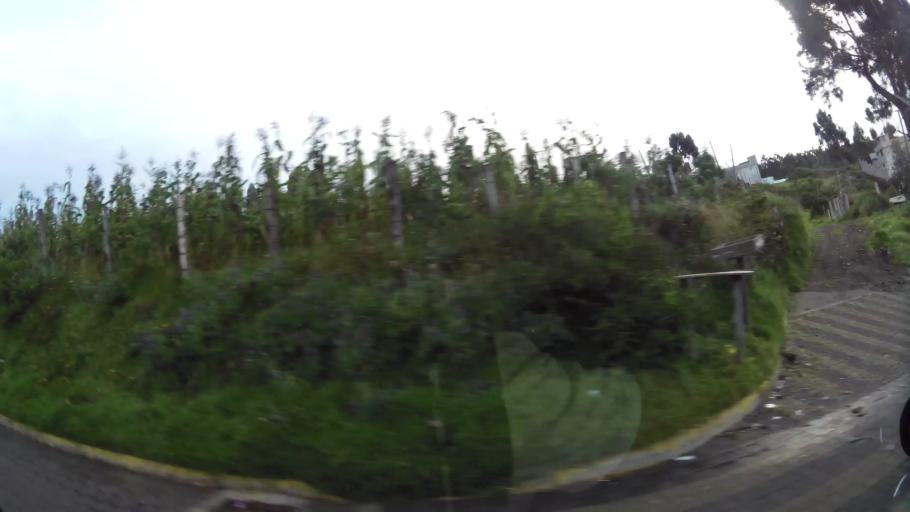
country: EC
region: Pichincha
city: Quito
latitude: -0.1042
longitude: -78.5253
